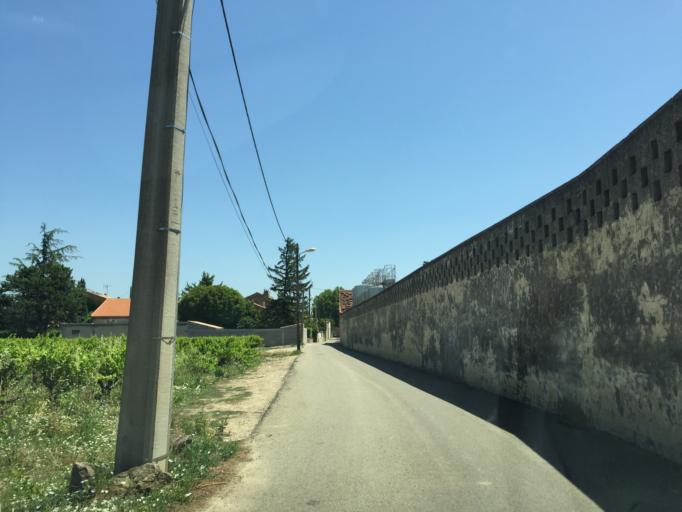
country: FR
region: Provence-Alpes-Cote d'Azur
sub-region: Departement du Vaucluse
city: Sainte-Cecile-les-Vignes
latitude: 44.2445
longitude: 4.8821
